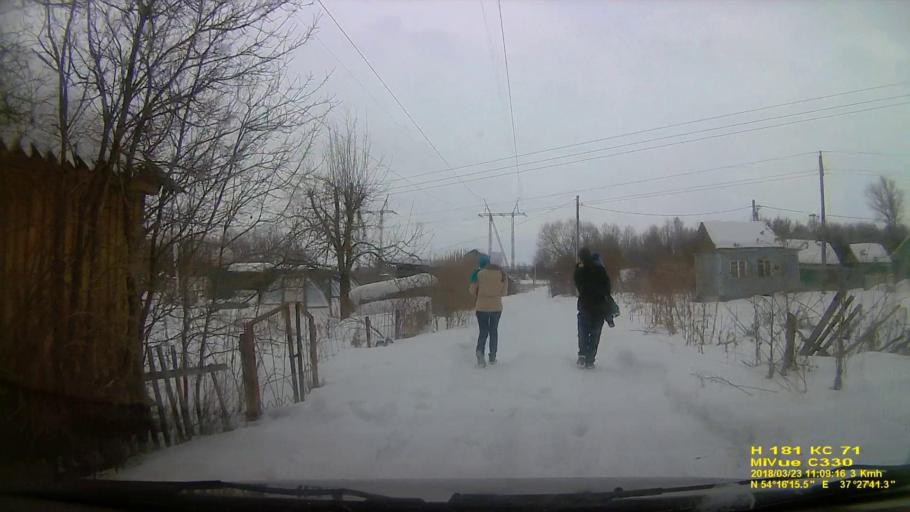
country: RU
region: Tula
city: Leninskiy
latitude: 54.2709
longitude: 37.4614
